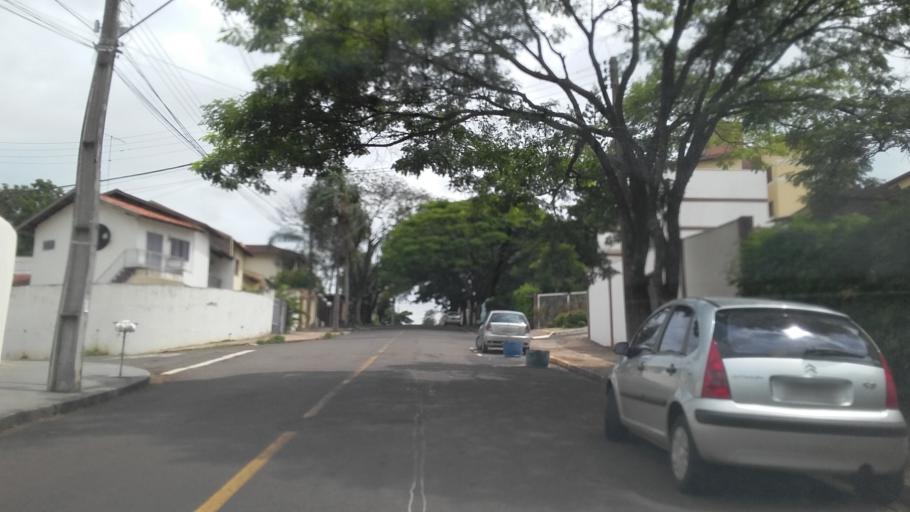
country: BR
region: Parana
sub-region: Londrina
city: Londrina
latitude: -23.3256
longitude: -51.1742
